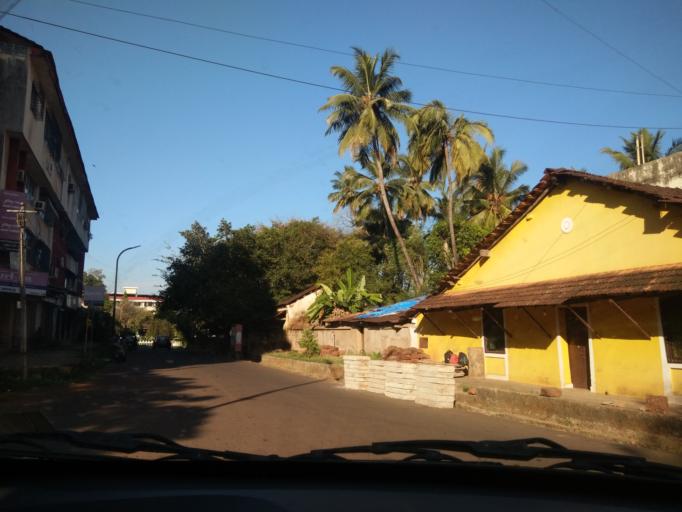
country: IN
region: Goa
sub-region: South Goa
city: Madgaon
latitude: 15.2777
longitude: 73.9580
